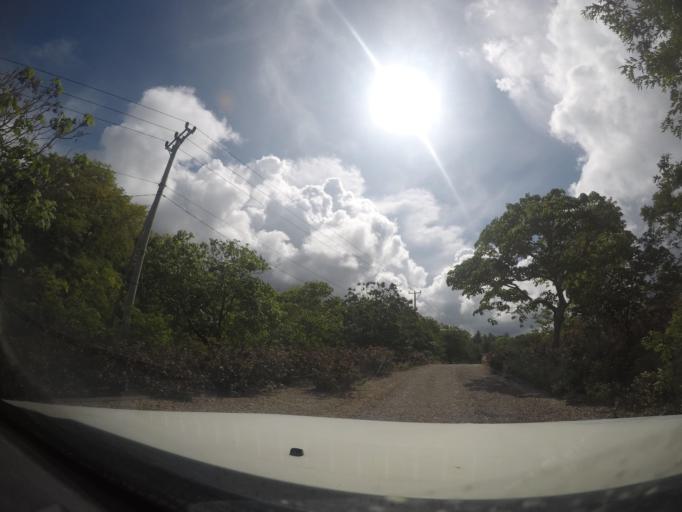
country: TL
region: Lautem
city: Lospalos
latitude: -8.3428
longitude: 127.0285
